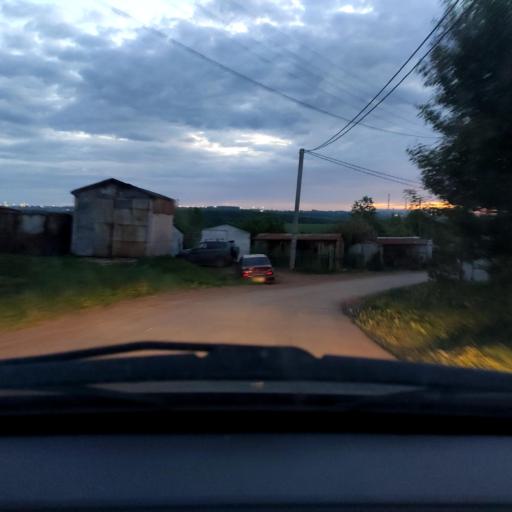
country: RU
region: Bashkortostan
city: Blagoveshchensk
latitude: 54.9013
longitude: 56.1447
